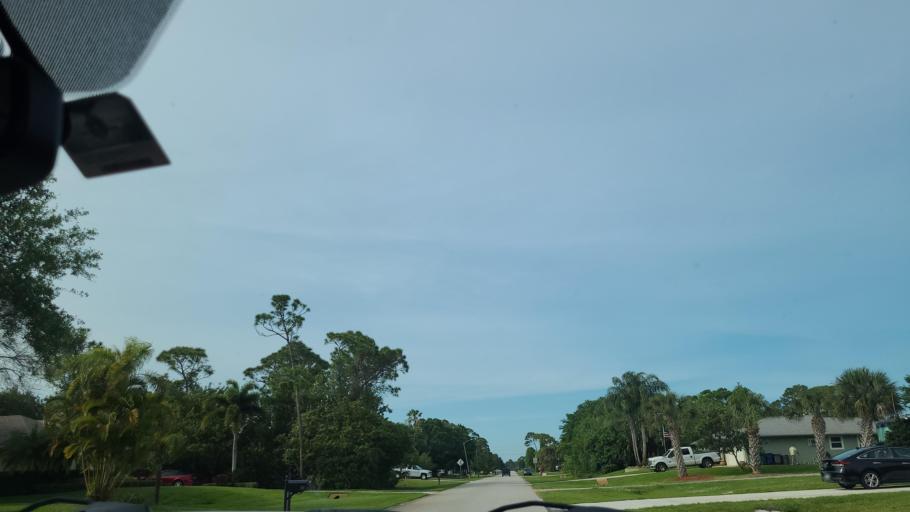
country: US
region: Florida
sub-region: Indian River County
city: Sebastian
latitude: 27.7951
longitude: -80.4717
